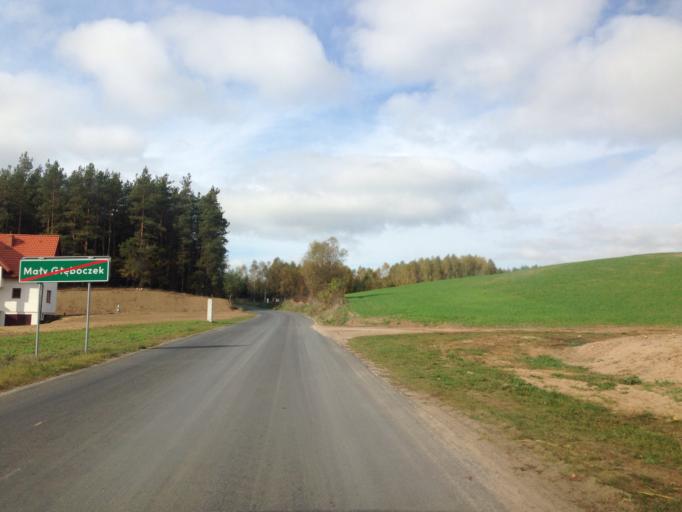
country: PL
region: Kujawsko-Pomorskie
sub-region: Powiat brodnicki
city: Brzozie
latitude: 53.3106
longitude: 19.5604
